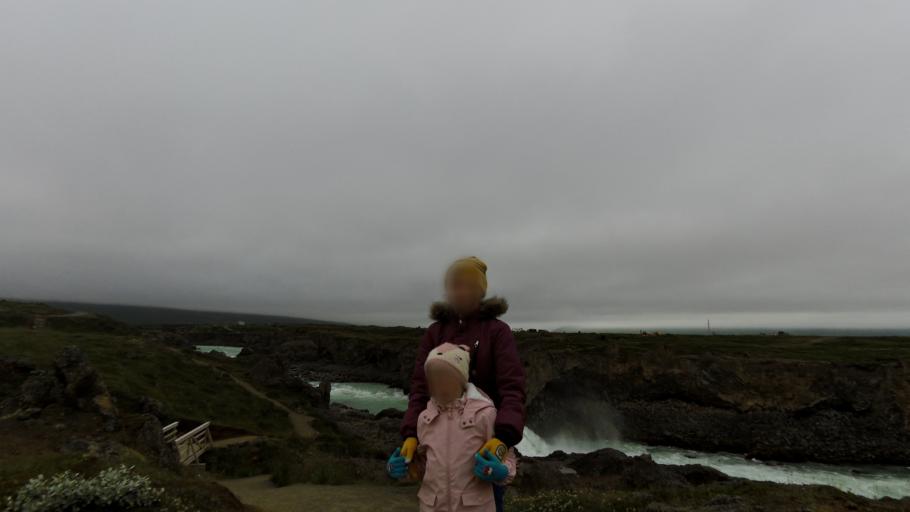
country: IS
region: Northeast
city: Laugar
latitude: 65.6848
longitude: -17.5405
